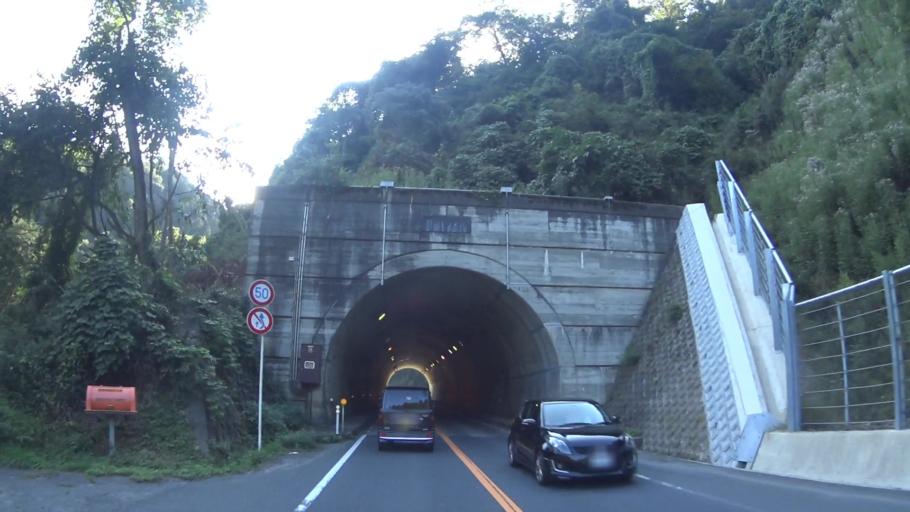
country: JP
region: Kyoto
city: Miyazu
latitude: 35.6633
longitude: 135.0131
